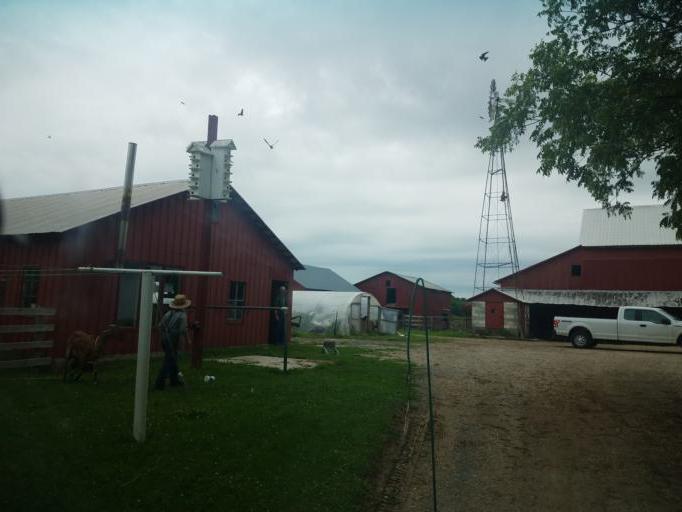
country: US
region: Ohio
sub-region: Hardin County
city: Kenton
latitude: 40.6177
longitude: -83.5122
